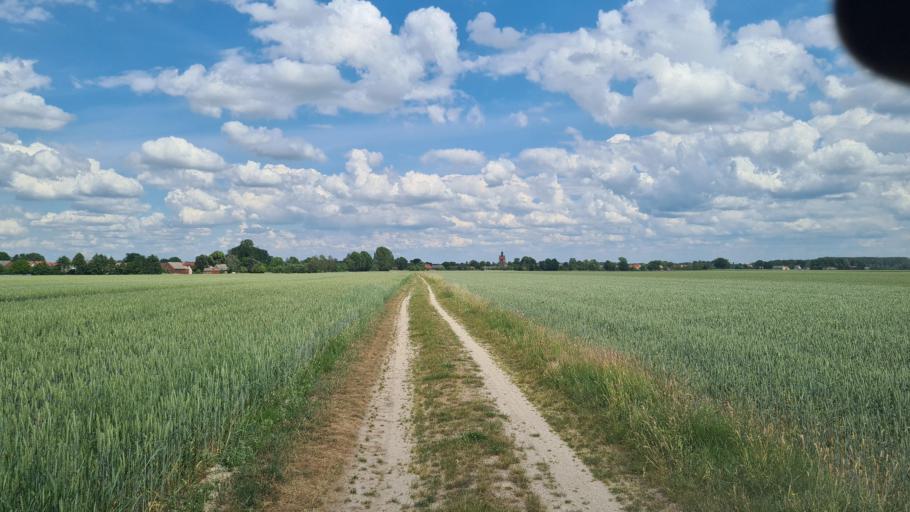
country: DE
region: Brandenburg
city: Doberlug-Kirchhain
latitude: 51.6495
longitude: 13.5203
